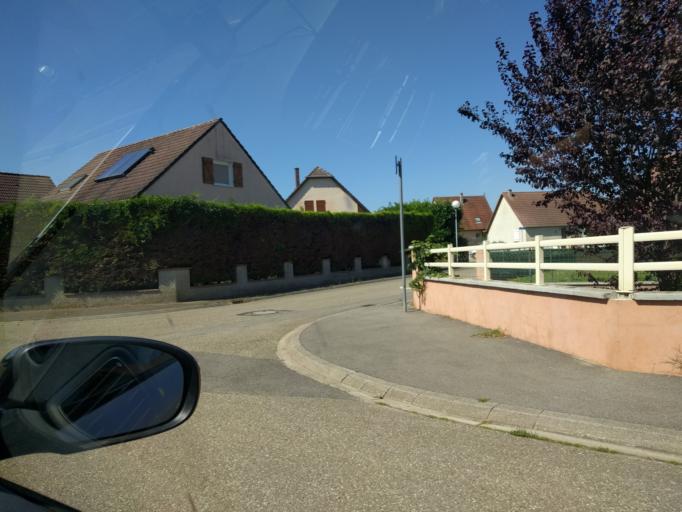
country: FR
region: Alsace
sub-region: Departement du Bas-Rhin
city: Geispolsheim
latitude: 48.5207
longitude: 7.6558
